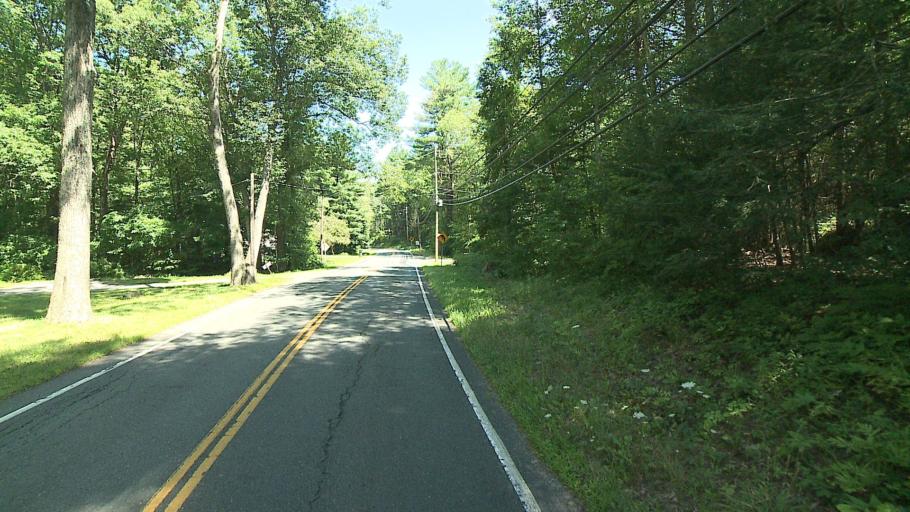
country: US
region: Connecticut
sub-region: Litchfield County
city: New Hartford Center
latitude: 41.9100
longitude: -72.9954
